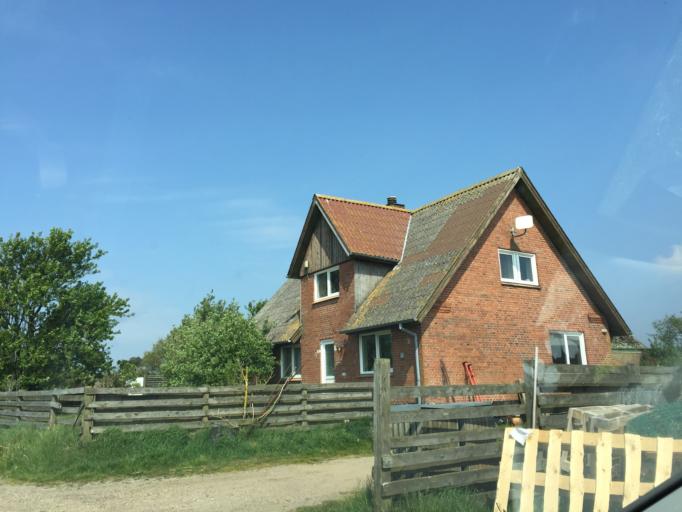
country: DK
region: South Denmark
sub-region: Esbjerg Kommune
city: Tjaereborg
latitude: 55.2791
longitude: 8.5411
